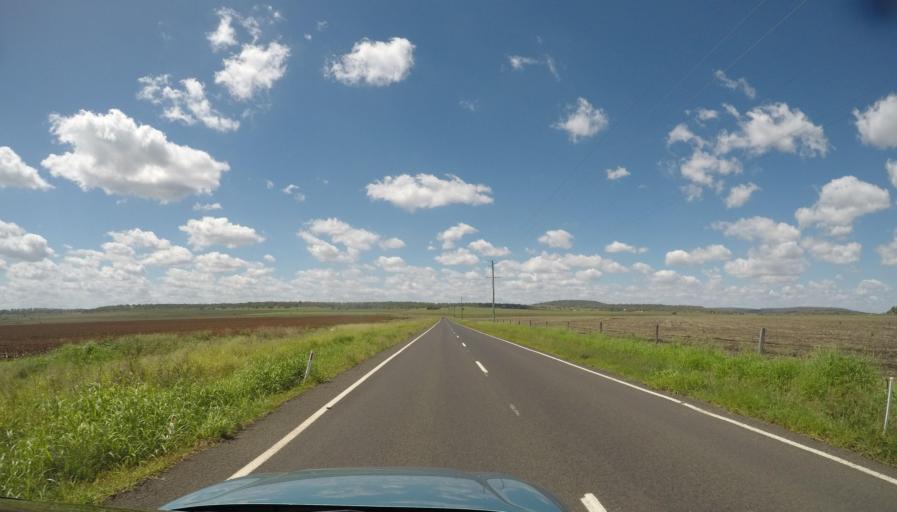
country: AU
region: Queensland
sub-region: Toowoomba
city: Oakey
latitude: -27.5408
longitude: 151.6444
